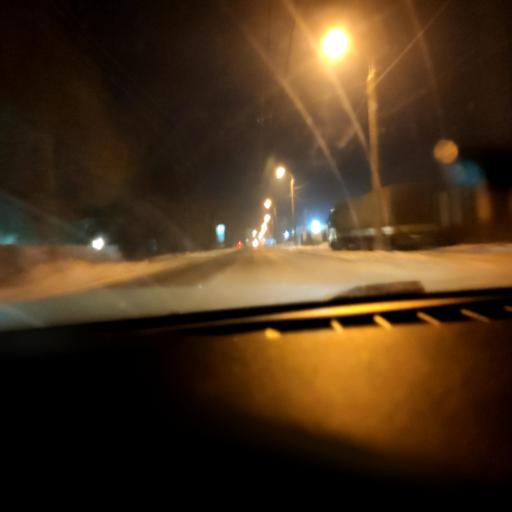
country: RU
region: Samara
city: Samara
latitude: 53.1990
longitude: 50.2680
